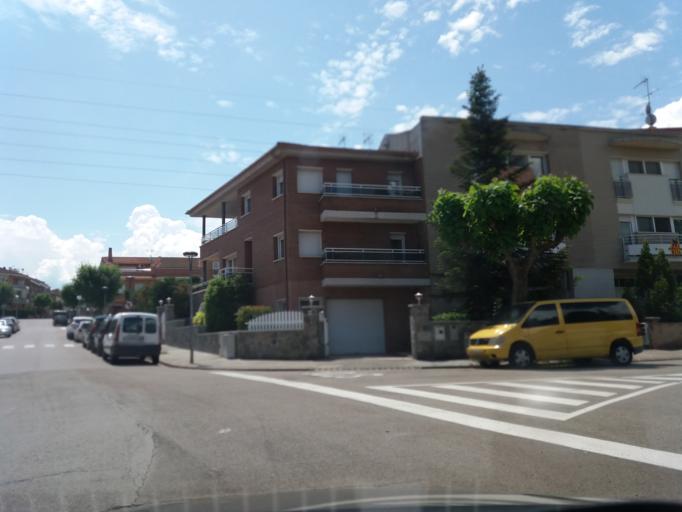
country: ES
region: Catalonia
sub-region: Provincia de Barcelona
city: Sant Joan de Vilatorrada
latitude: 41.7392
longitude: 1.7987
